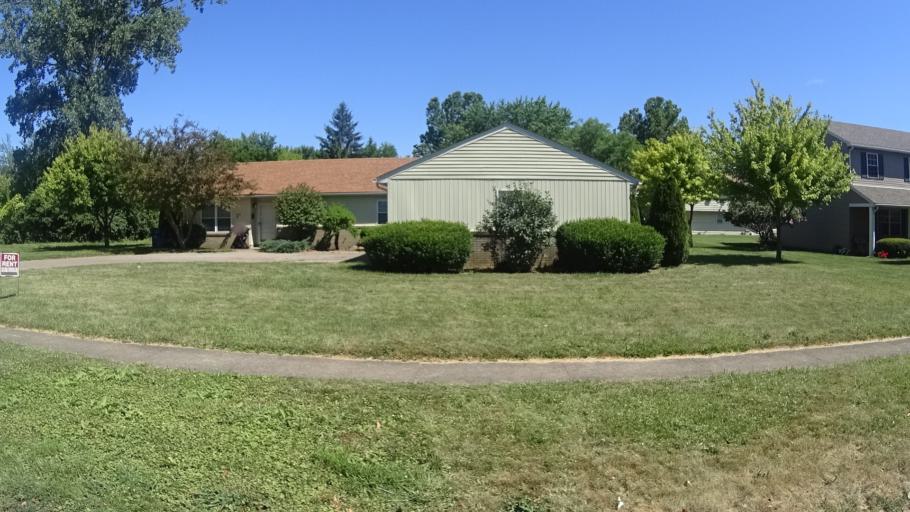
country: US
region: Ohio
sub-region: Erie County
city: Sandusky
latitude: 41.4328
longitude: -82.6710
